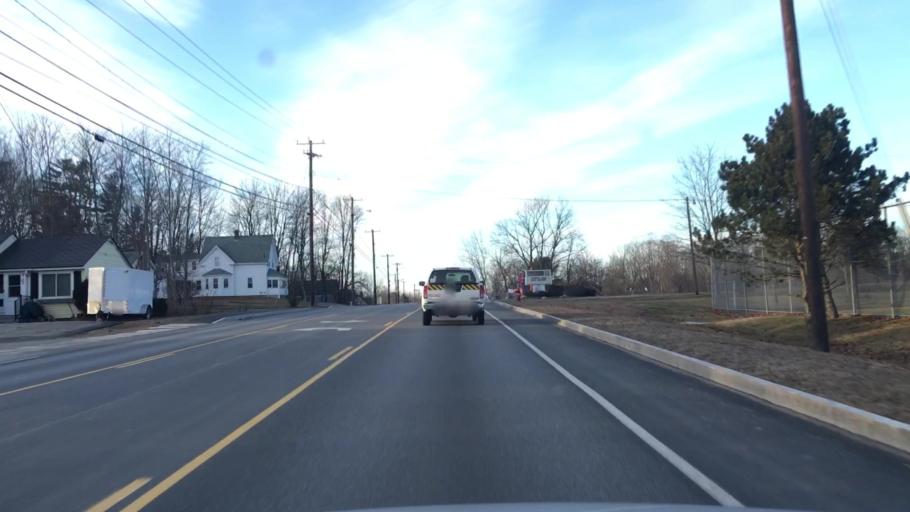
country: US
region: Maine
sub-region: Hancock County
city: Ellsworth
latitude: 44.5552
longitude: -68.4318
